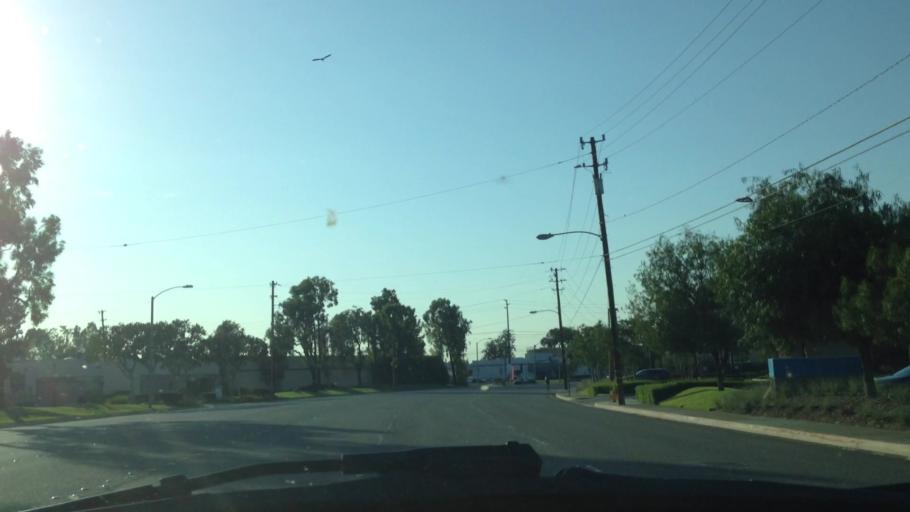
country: US
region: California
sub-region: Orange County
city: Placentia
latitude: 33.8608
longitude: -117.8406
